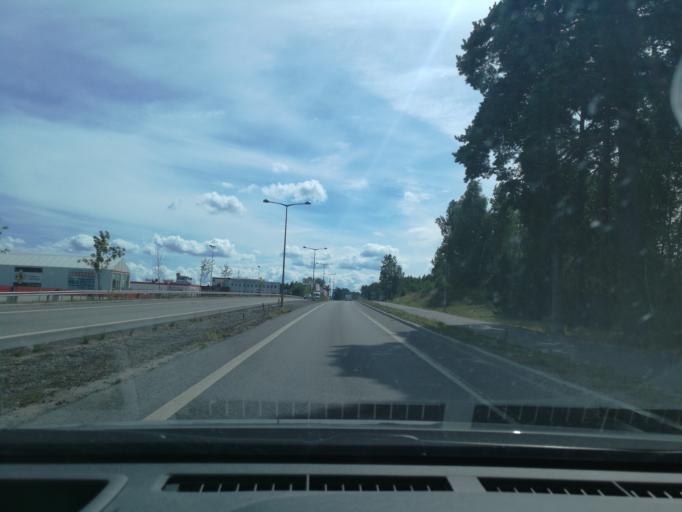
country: SE
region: Stockholm
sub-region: Upplands Vasby Kommun
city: Upplands Vaesby
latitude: 59.5008
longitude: 17.9221
